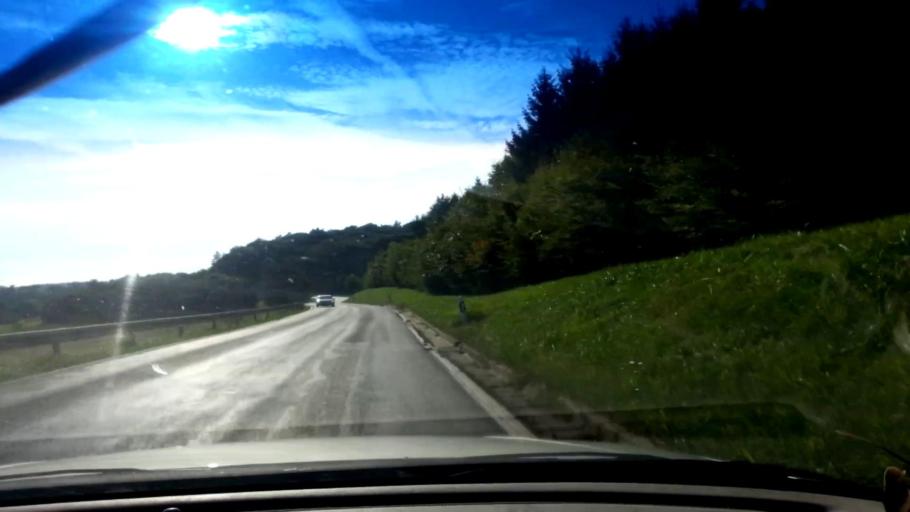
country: DE
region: Bavaria
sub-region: Upper Franconia
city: Baunach
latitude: 49.9753
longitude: 10.8196
